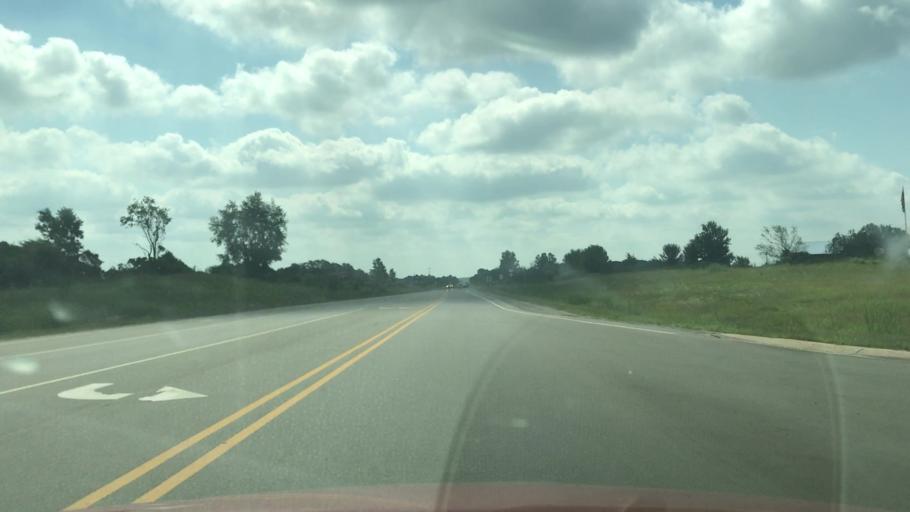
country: US
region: Michigan
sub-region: Kent County
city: Kent City
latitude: 43.2222
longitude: -85.7708
